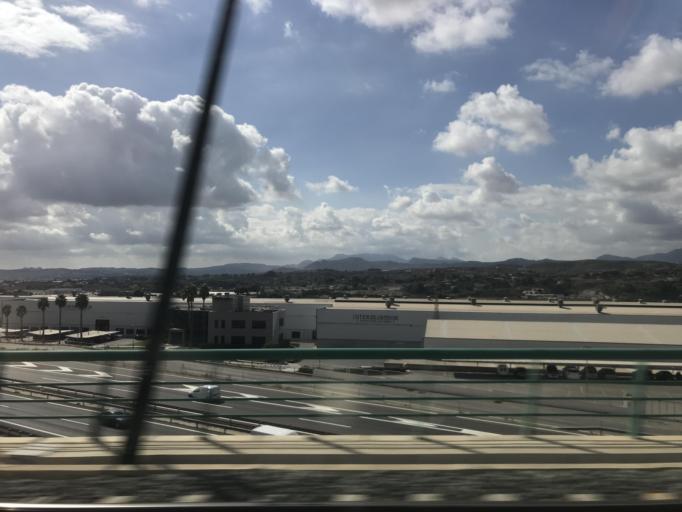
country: ES
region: Valencia
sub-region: Provincia de Alicante
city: Novelda
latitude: 38.4105
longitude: -0.7775
